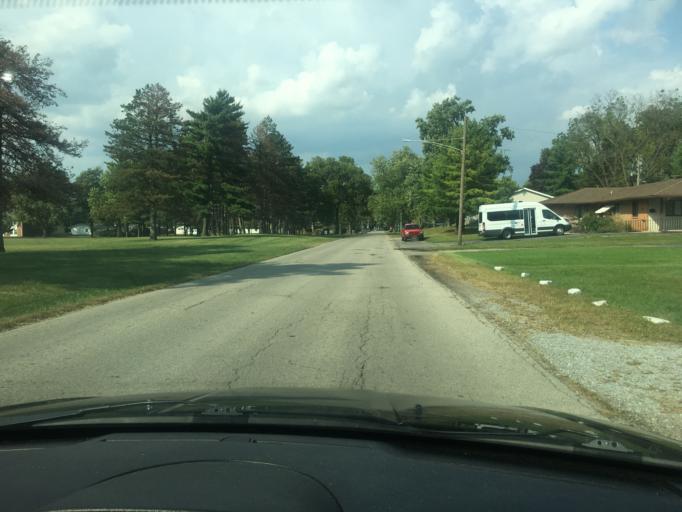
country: US
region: Ohio
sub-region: Champaign County
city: Urbana
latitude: 40.0989
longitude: -83.7566
